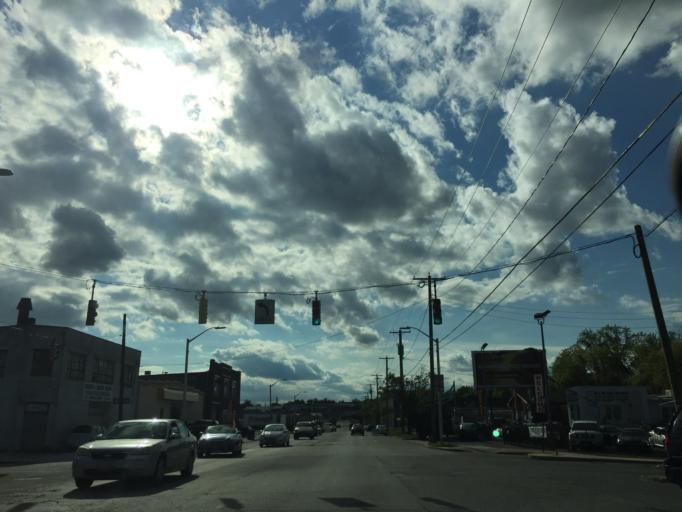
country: US
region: Maryland
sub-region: City of Baltimore
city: Baltimore
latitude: 39.3173
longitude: -76.5979
